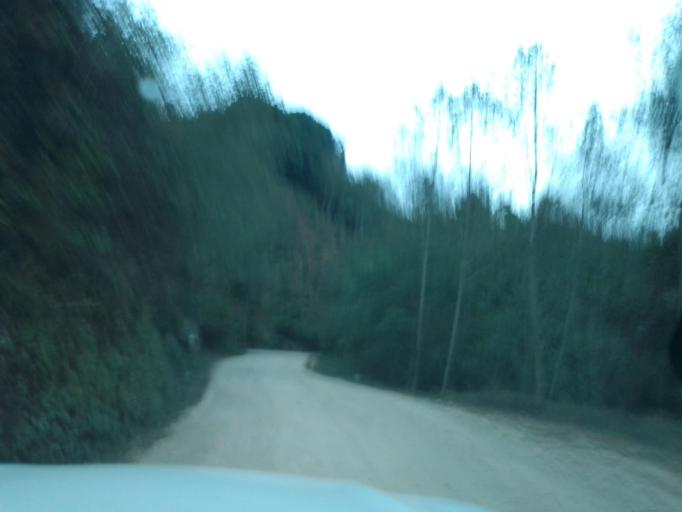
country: MX
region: Chiapas
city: Motozintla de Mendoza
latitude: 15.2292
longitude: -92.2380
